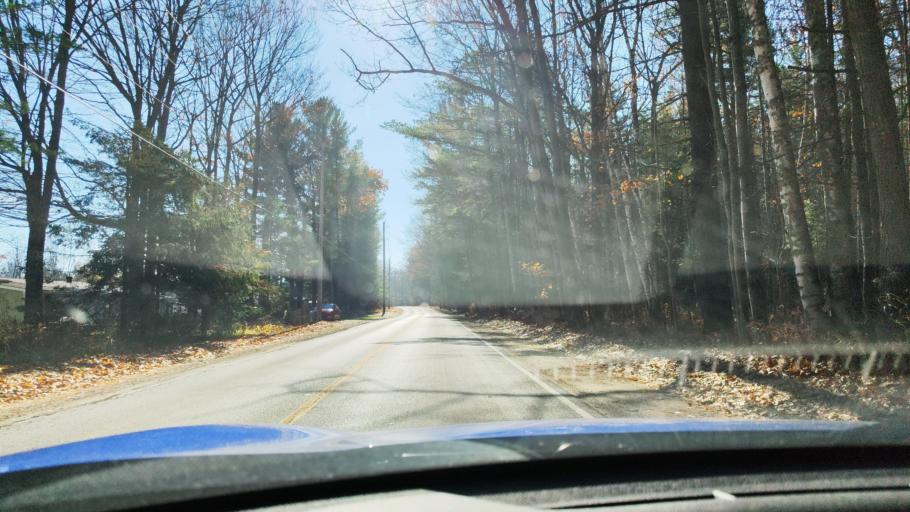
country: CA
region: Ontario
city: Wasaga Beach
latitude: 44.4919
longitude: -80.0048
